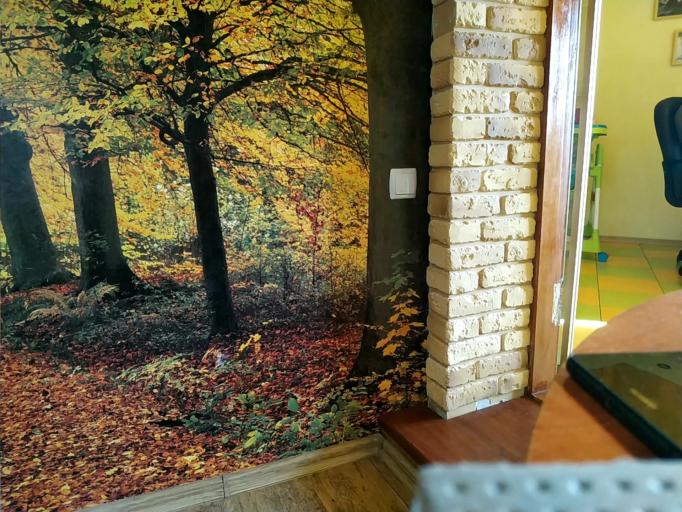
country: RU
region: Tverskaya
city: Zubtsov
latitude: 56.2057
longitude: 34.5965
